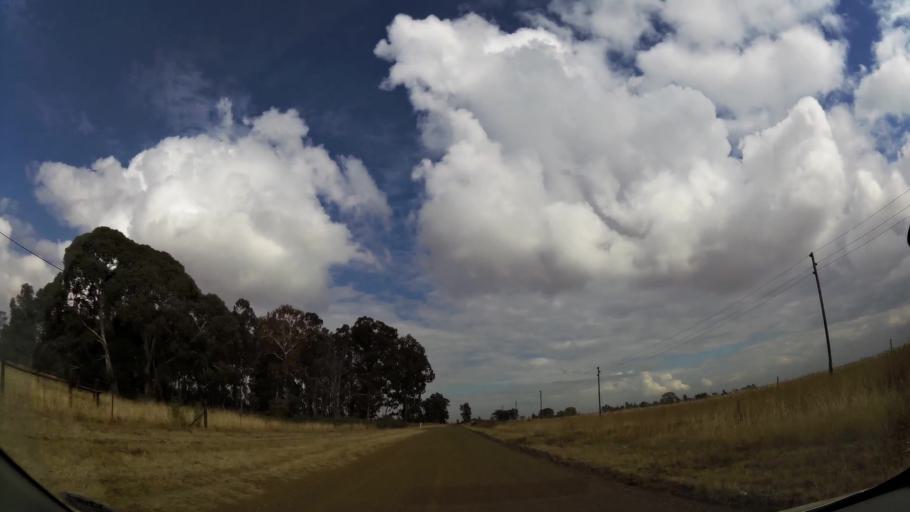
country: ZA
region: Gauteng
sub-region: Sedibeng District Municipality
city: Meyerton
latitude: -26.6023
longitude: 28.0810
